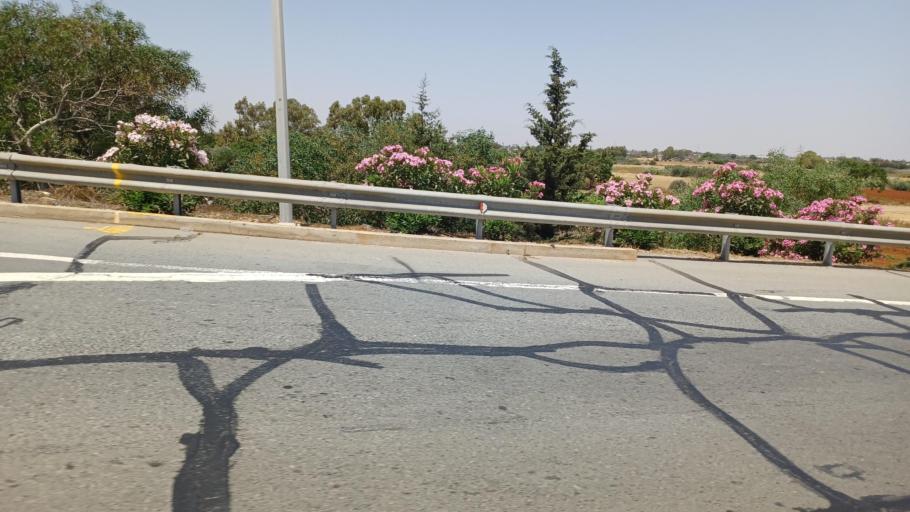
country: CY
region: Ammochostos
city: Liopetri
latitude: 34.9858
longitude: 33.9278
